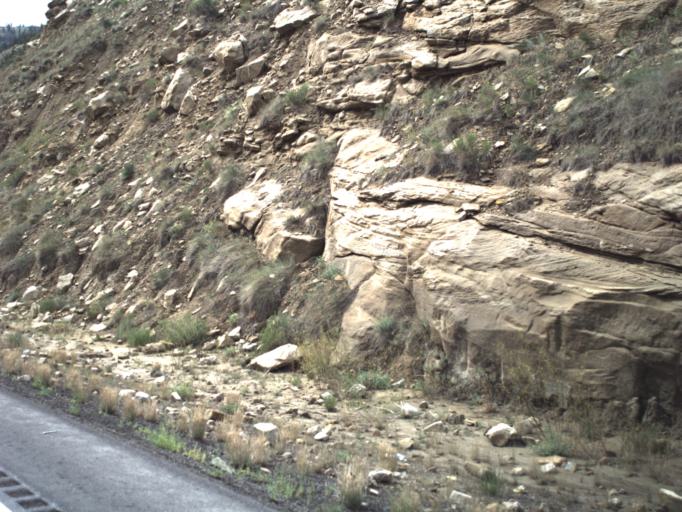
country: US
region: Utah
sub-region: Carbon County
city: Helper
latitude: 39.7680
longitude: -110.9067
